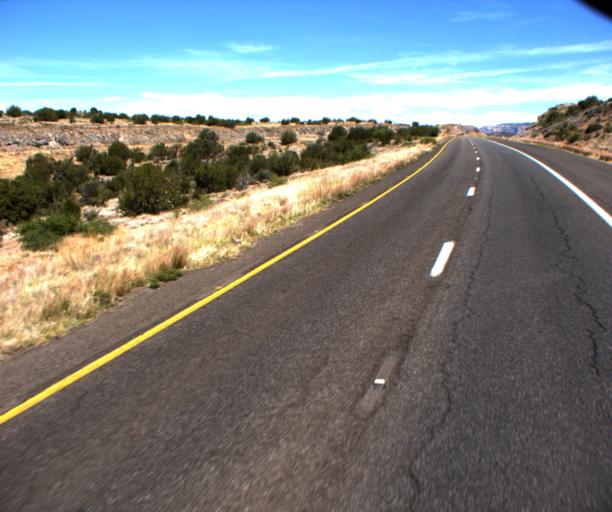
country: US
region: Arizona
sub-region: Yavapai County
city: Cornville
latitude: 34.8019
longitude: -111.9114
